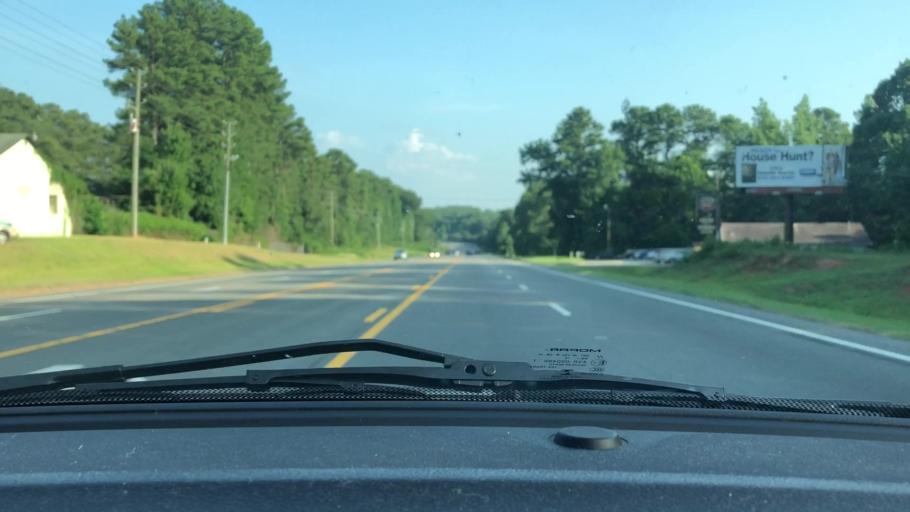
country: US
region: North Carolina
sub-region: Lee County
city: Broadway
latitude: 35.4086
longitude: -79.1157
